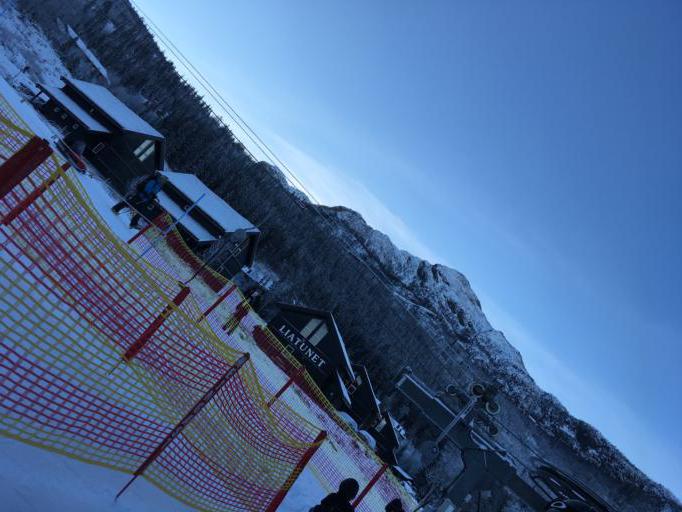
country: NO
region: Buskerud
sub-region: Hemsedal
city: Hemsedal
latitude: 60.8626
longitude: 8.5139
